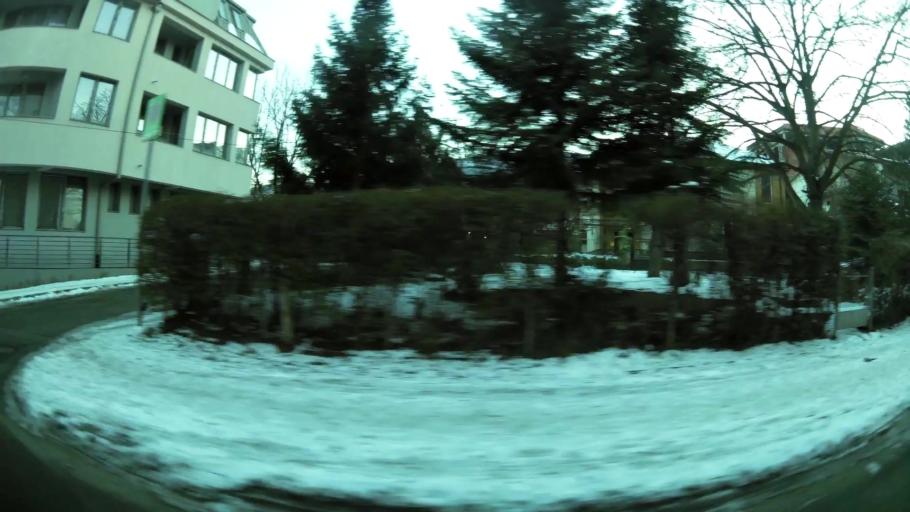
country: MK
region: Karpos
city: Skopje
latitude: 41.9916
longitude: 21.4159
